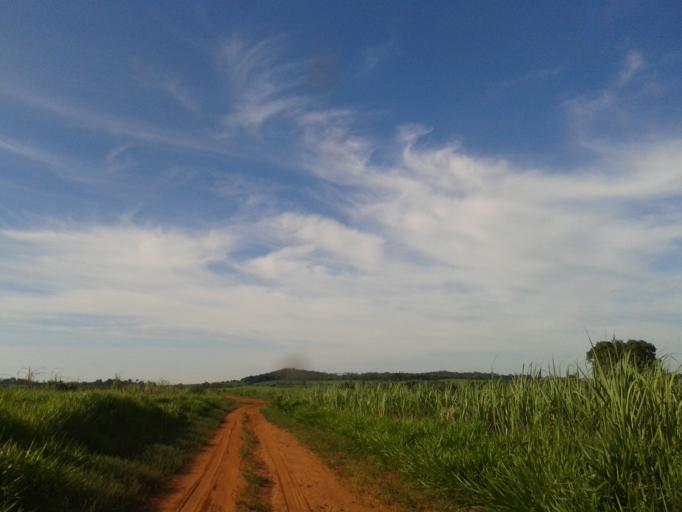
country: BR
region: Minas Gerais
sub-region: Santa Vitoria
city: Santa Vitoria
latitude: -19.0989
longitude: -49.9904
